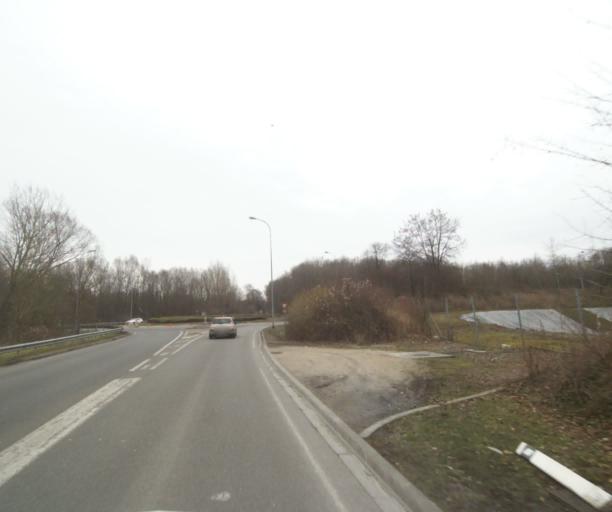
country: FR
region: Lorraine
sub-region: Departement de la Meuse
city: Ancerville
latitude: 48.6234
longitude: 4.9929
